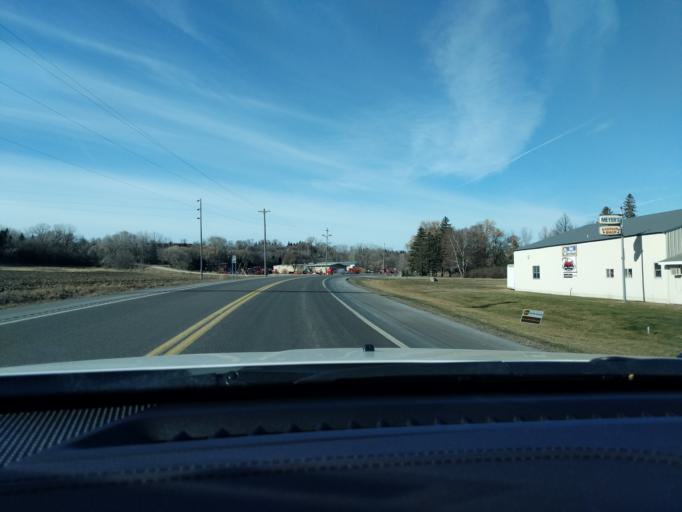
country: US
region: Minnesota
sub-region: Yellow Medicine County
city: Granite Falls
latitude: 44.8074
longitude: -95.5733
